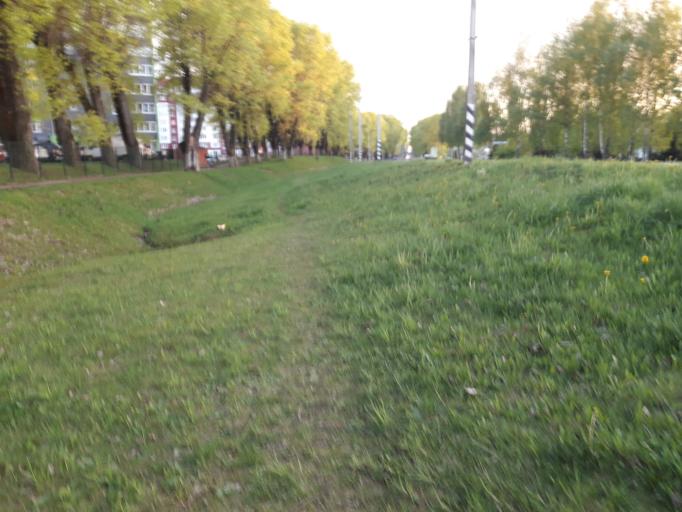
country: BY
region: Minsk
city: Syenitsa
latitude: 53.8239
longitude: 27.5295
